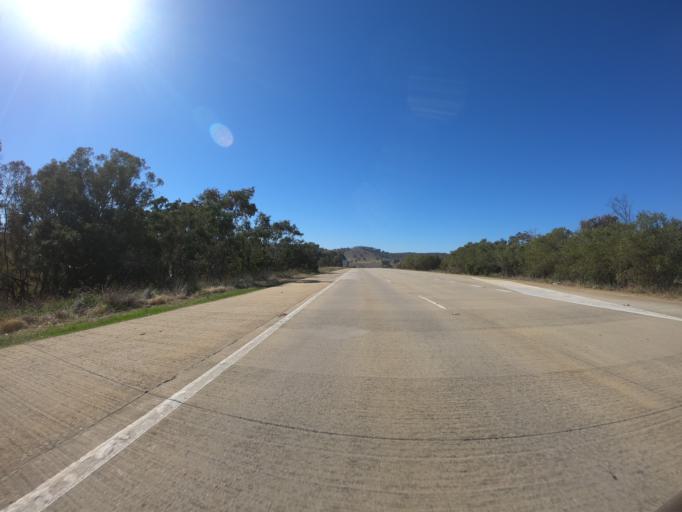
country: AU
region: New South Wales
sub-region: Yass Valley
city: Gundaroo
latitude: -35.1799
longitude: 149.2647
